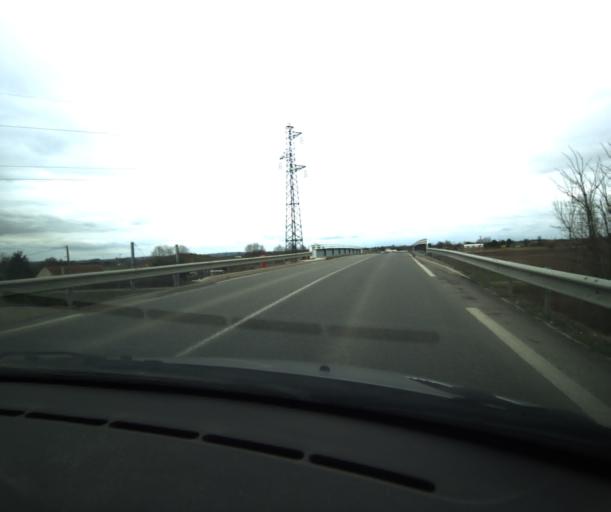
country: FR
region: Midi-Pyrenees
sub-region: Departement du Tarn-et-Garonne
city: Castelsarrasin
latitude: 44.0644
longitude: 1.1048
